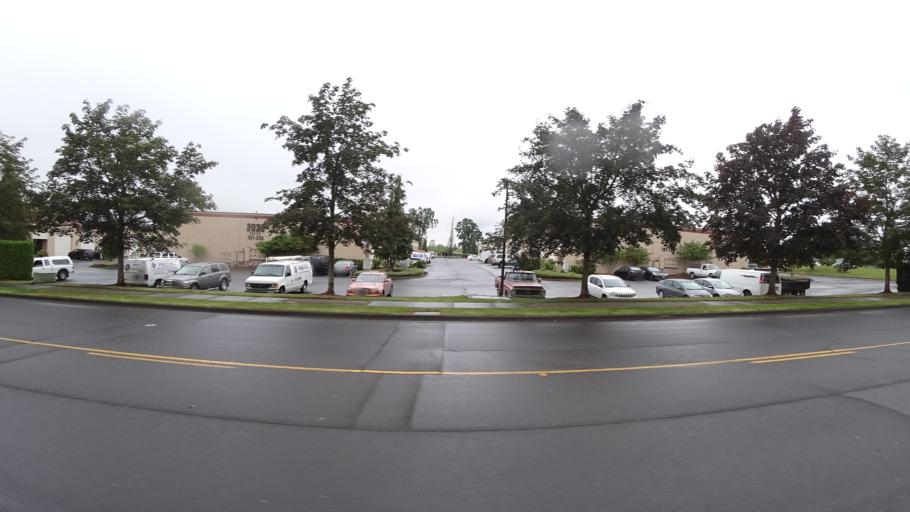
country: US
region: Oregon
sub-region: Washington County
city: Rockcreek
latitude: 45.5348
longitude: -122.8985
